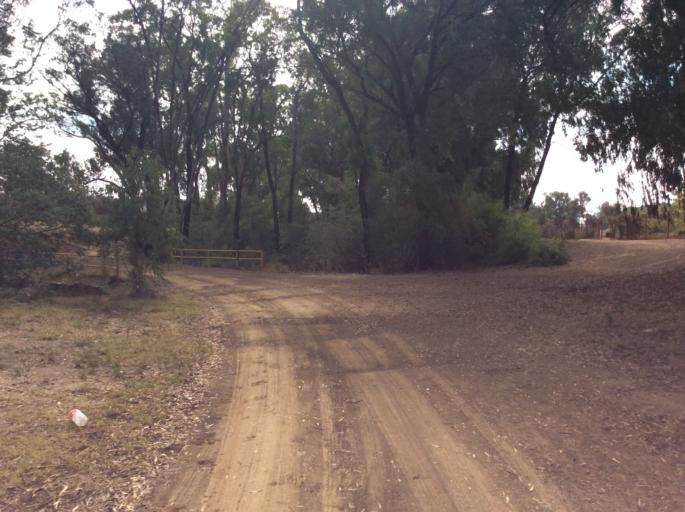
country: ZA
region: Orange Free State
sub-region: Xhariep District Municipality
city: Dewetsdorp
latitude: -29.5903
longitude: 26.6652
